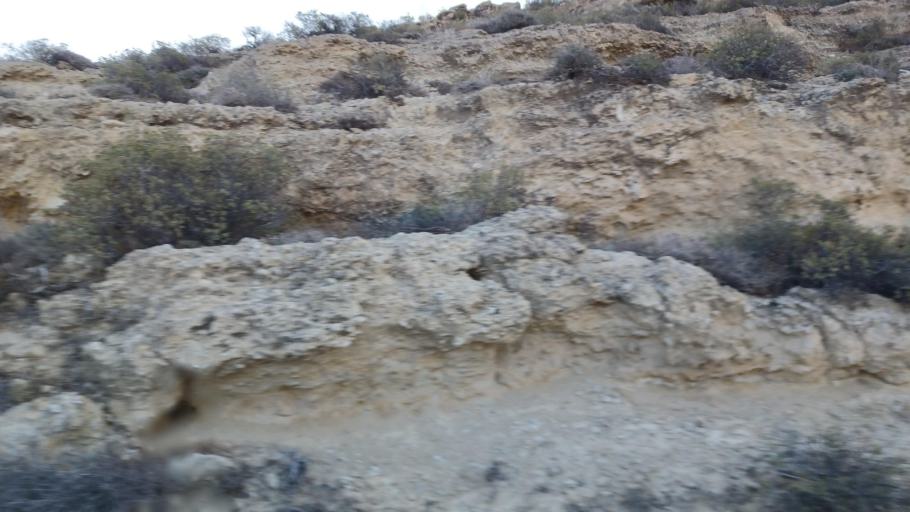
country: CY
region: Larnaka
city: Pyla
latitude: 34.9915
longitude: 33.7113
